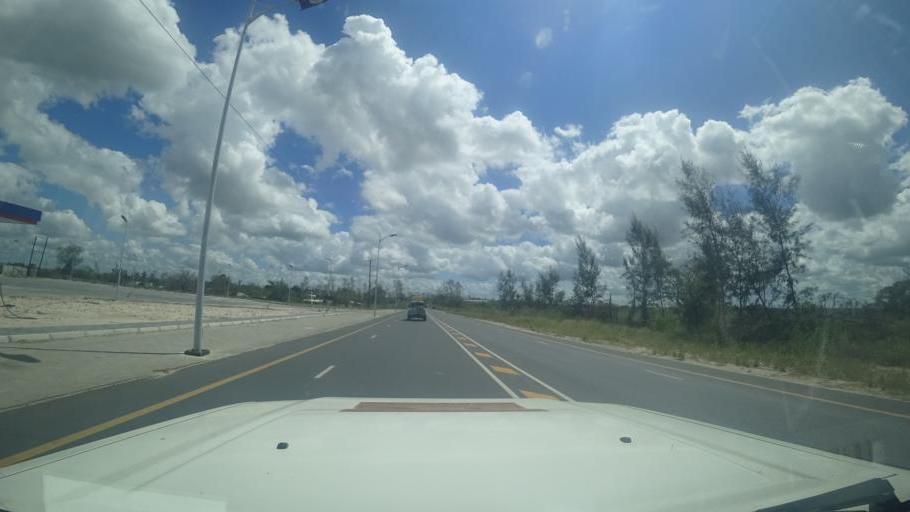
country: MZ
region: Sofala
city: Dondo
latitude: -19.5746
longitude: 34.7193
